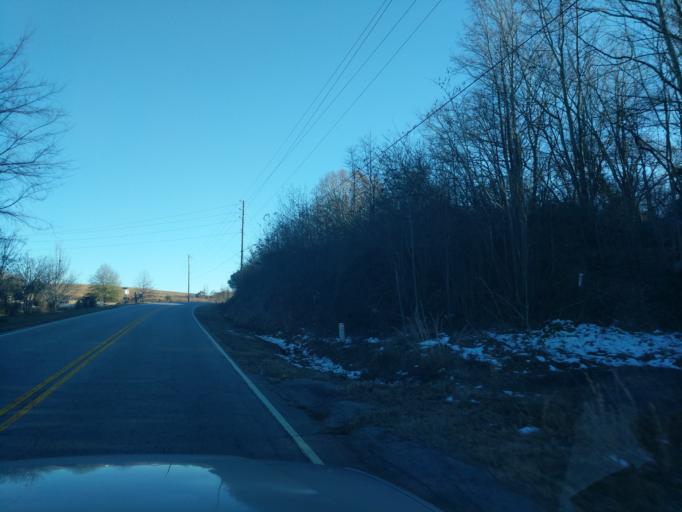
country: US
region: South Carolina
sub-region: Oconee County
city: Westminster
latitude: 34.7188
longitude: -83.2069
